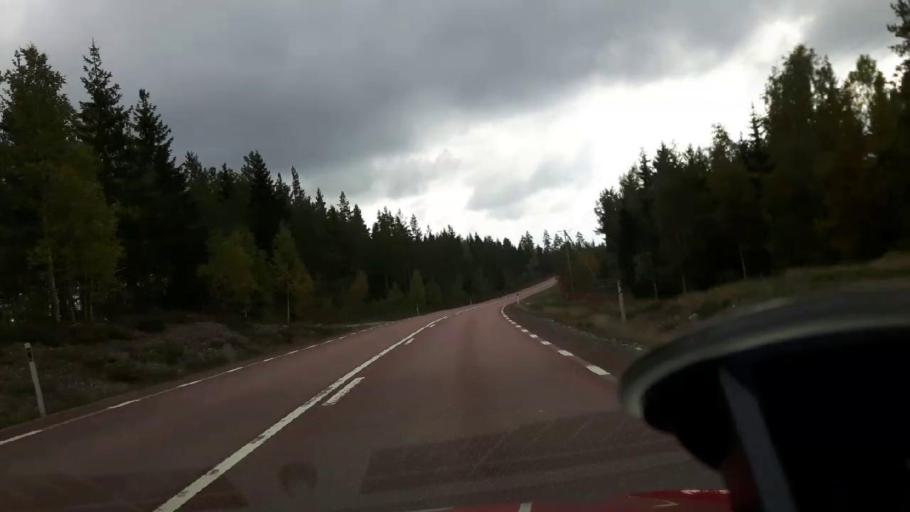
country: SE
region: Gaevleborg
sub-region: Soderhamns Kommun
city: Soderhamn
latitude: 61.1235
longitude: 16.9337
